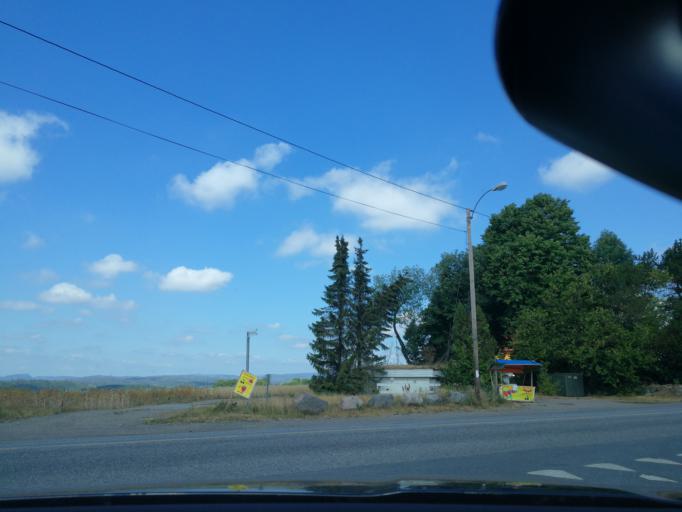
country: NO
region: Vestfold
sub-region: Sandefjord
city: Sandefjord
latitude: 59.1558
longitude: 10.1994
